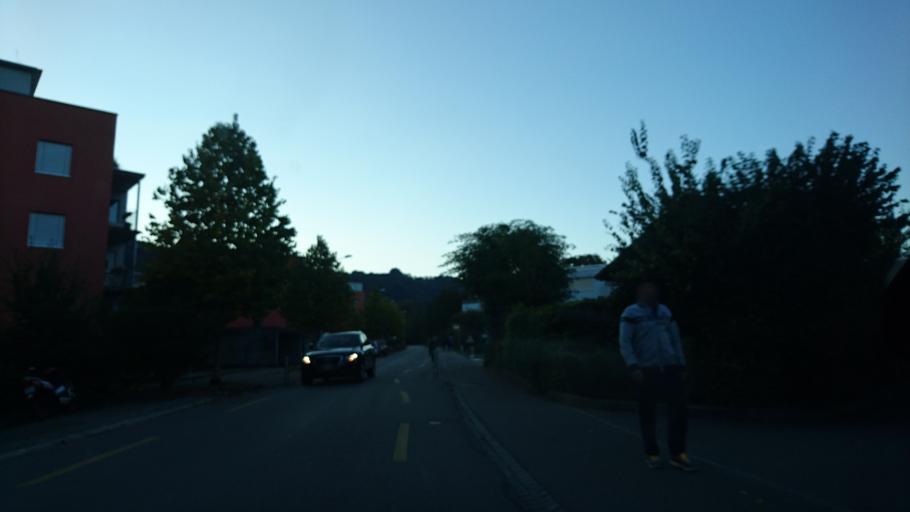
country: CH
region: Bern
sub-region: Bern-Mittelland District
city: Munsingen
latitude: 46.8738
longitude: 7.5526
